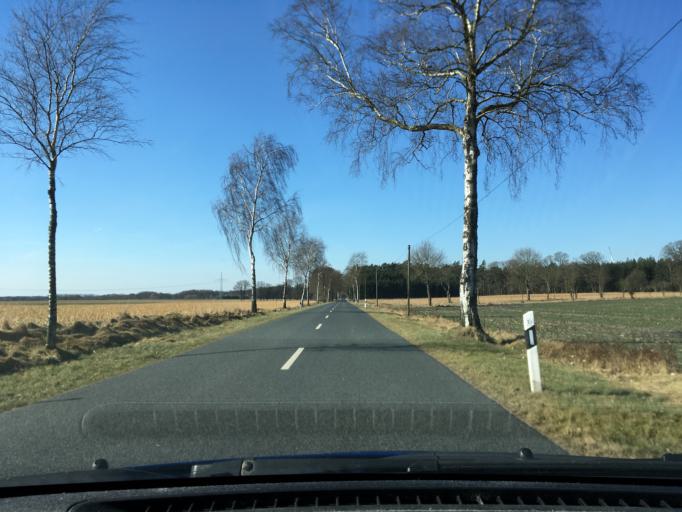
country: DE
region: Lower Saxony
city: Neuenkirchen
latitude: 53.0713
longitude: 9.6943
